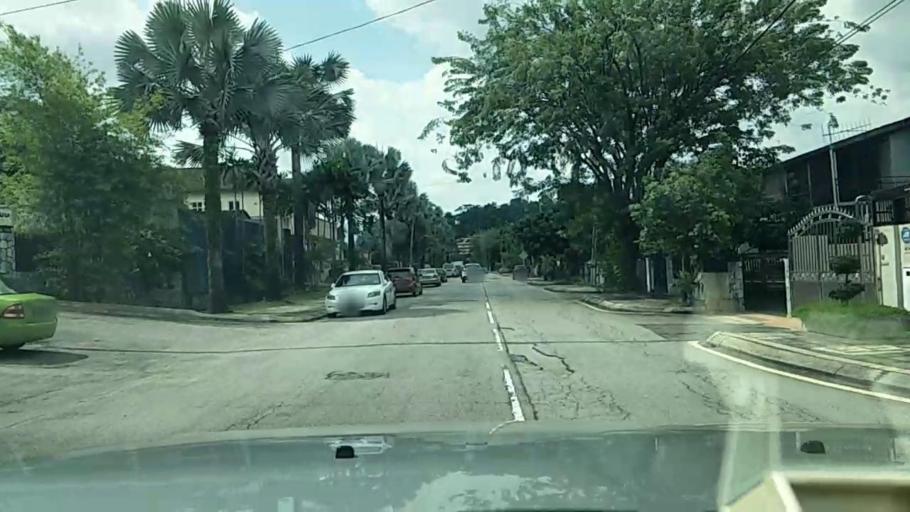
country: MY
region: Kuala Lumpur
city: Kuala Lumpur
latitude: 3.1337
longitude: 101.6734
